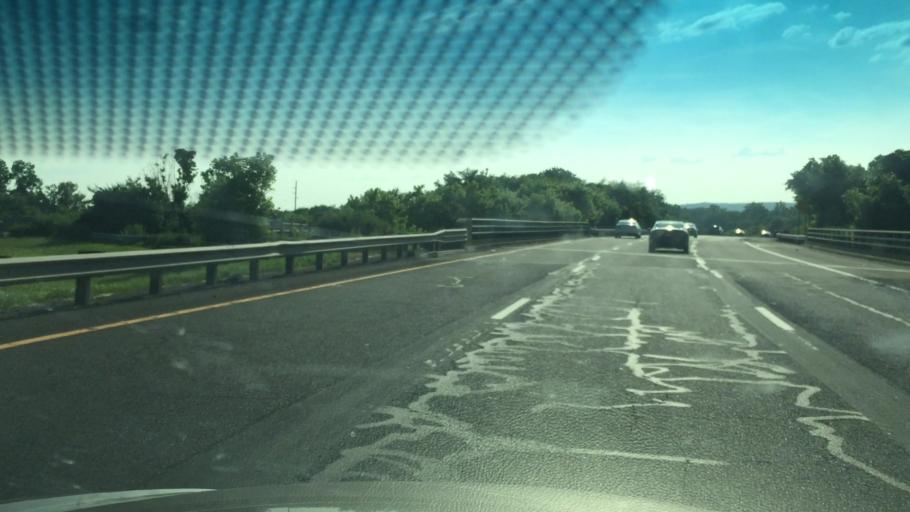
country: US
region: New Jersey
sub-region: Warren County
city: Hackettstown
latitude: 40.9196
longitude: -74.8425
